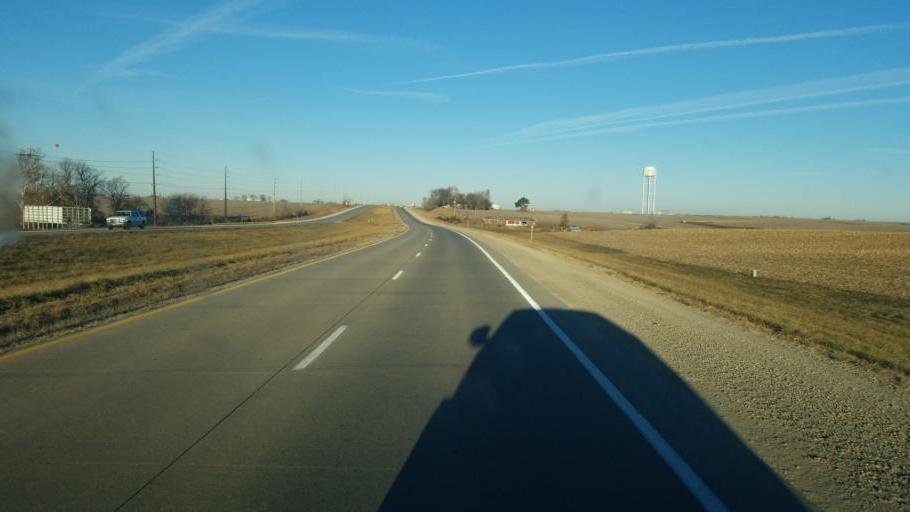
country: US
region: Iowa
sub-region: Mahaska County
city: Oskaloosa
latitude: 41.3299
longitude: -92.7159
